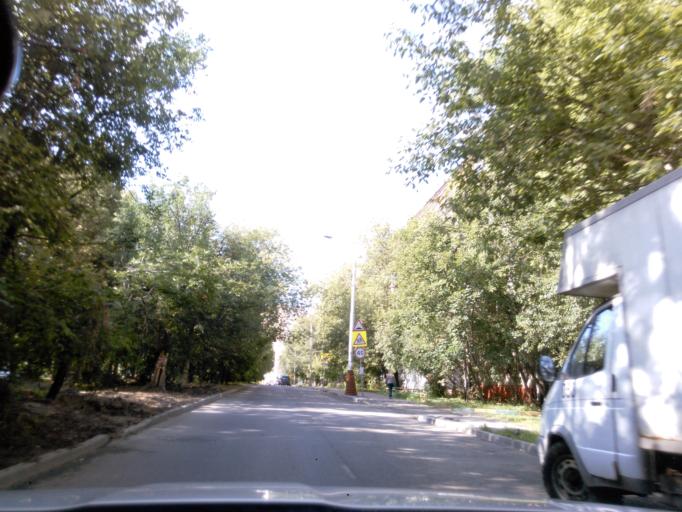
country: RU
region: Moskovskaya
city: Koptevo
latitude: 55.8302
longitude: 37.5252
